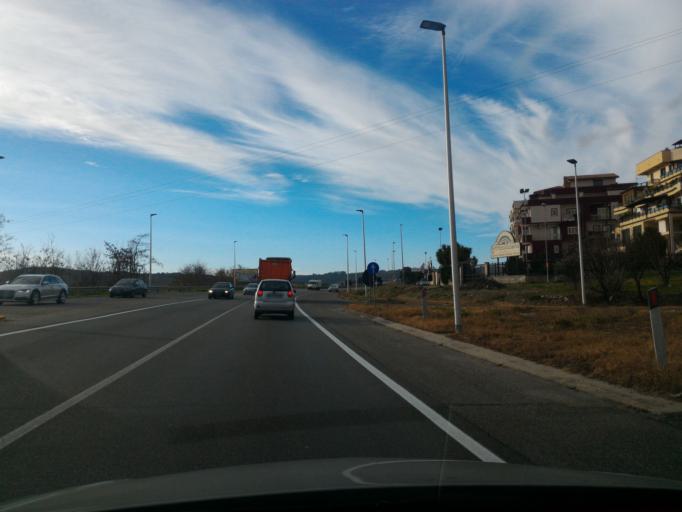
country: IT
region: Calabria
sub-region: Provincia di Crotone
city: Crotone
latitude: 39.0628
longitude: 17.1008
